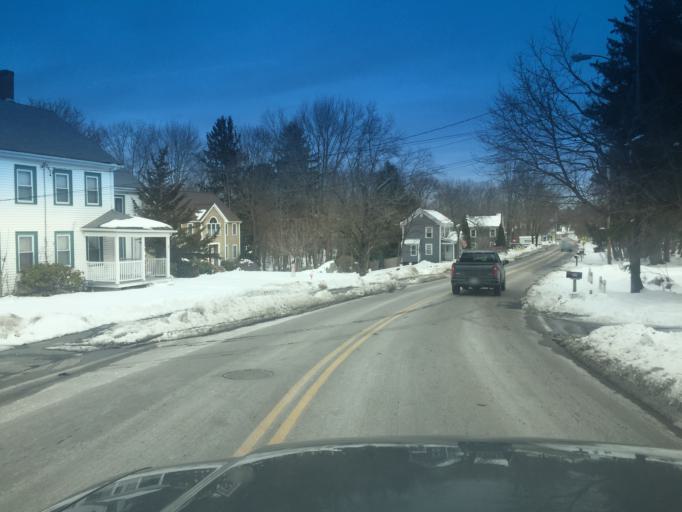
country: US
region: Massachusetts
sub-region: Norfolk County
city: Walpole
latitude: 42.1043
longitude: -71.2664
